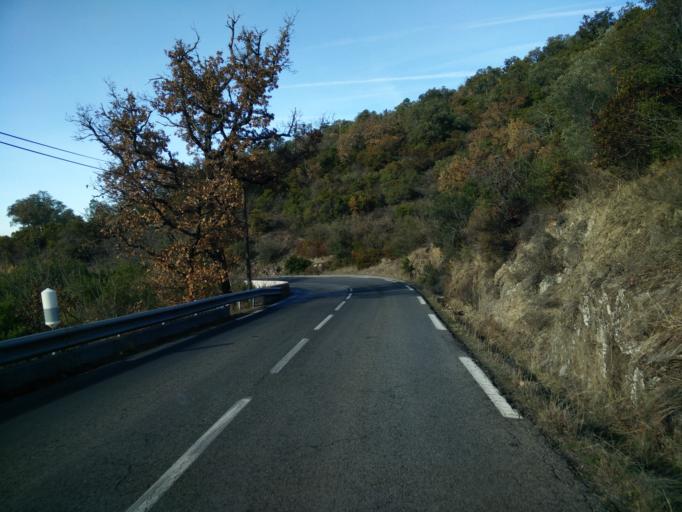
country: FR
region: Provence-Alpes-Cote d'Azur
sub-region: Departement du Var
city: La Garde-Freinet
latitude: 43.3318
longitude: 6.4378
